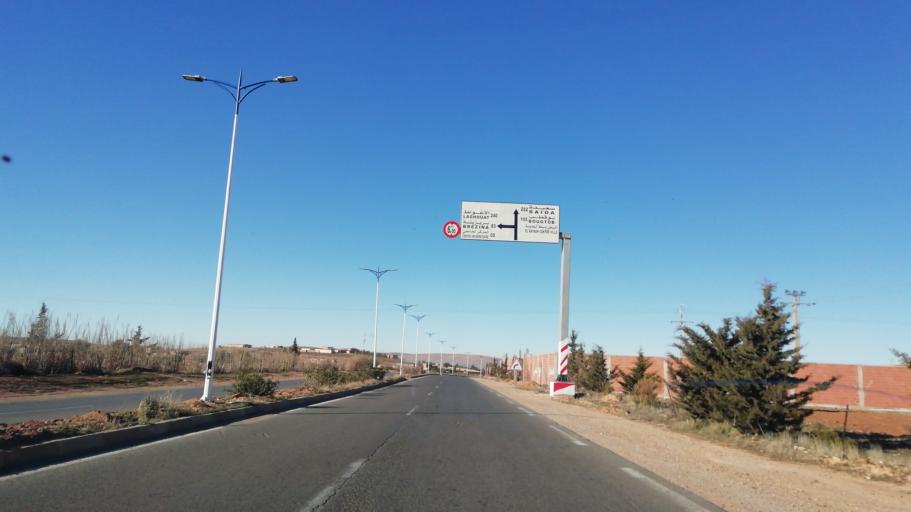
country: DZ
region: El Bayadh
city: El Bayadh
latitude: 33.6880
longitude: 1.0576
